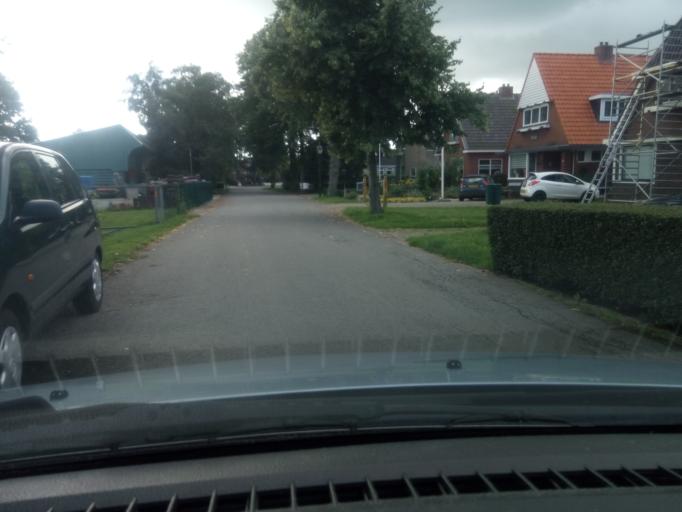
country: NL
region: Groningen
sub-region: Gemeente Zuidhorn
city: Grijpskerk
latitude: 53.2656
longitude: 6.2512
